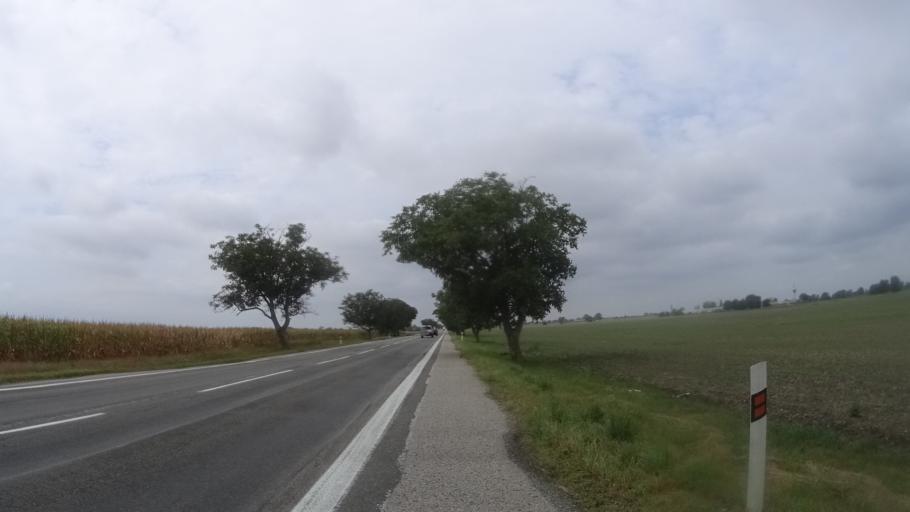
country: HU
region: Komarom-Esztergom
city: Acs
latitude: 47.7666
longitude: 18.0083
